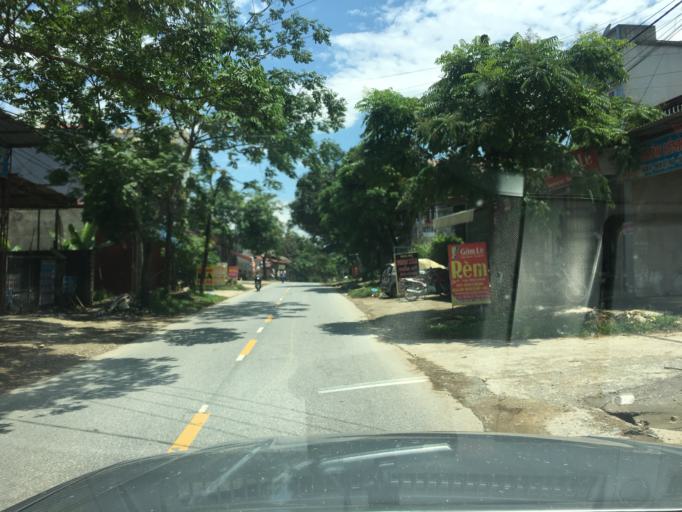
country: VN
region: Yen Bai
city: Son Thinh
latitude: 21.6174
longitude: 104.5082
